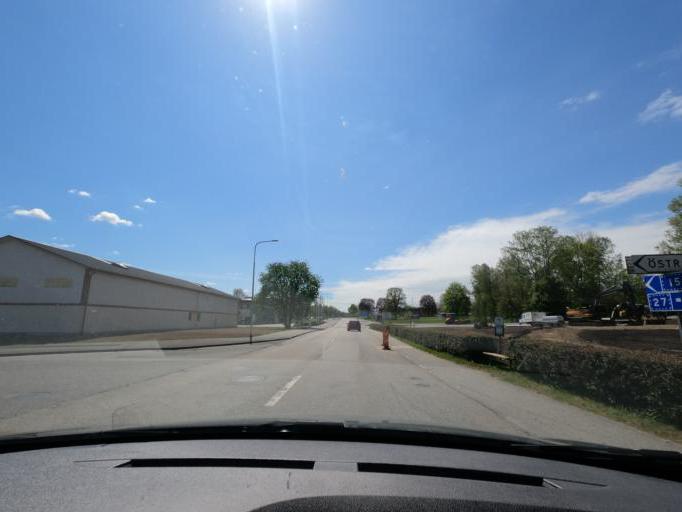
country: SE
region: Joenkoeping
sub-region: Varnamo Kommun
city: Bredaryd
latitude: 57.1741
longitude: 13.7405
